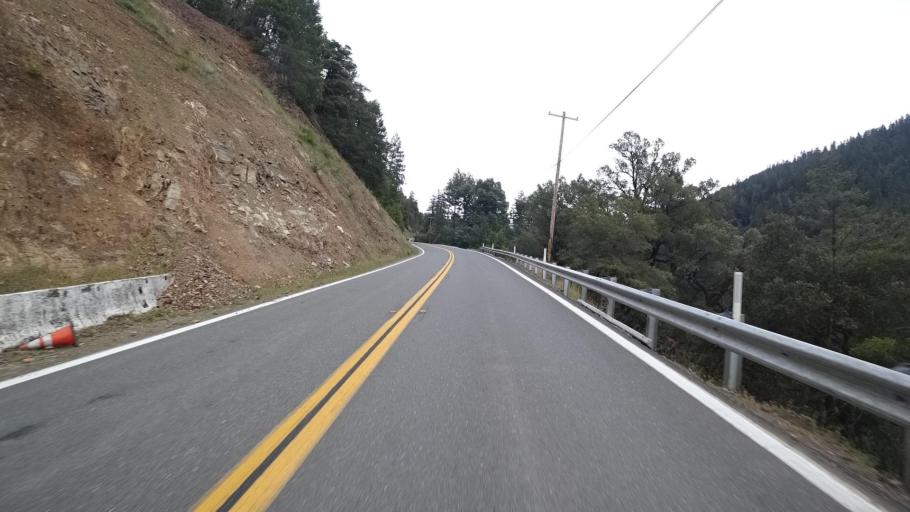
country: US
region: California
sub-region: Humboldt County
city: Willow Creek
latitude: 40.9948
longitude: -123.6307
